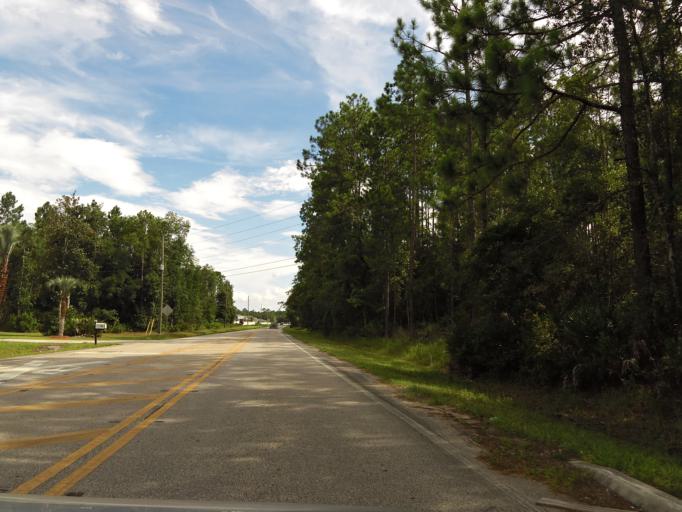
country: US
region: Florida
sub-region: Clay County
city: Green Cove Springs
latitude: 30.0283
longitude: -81.7192
